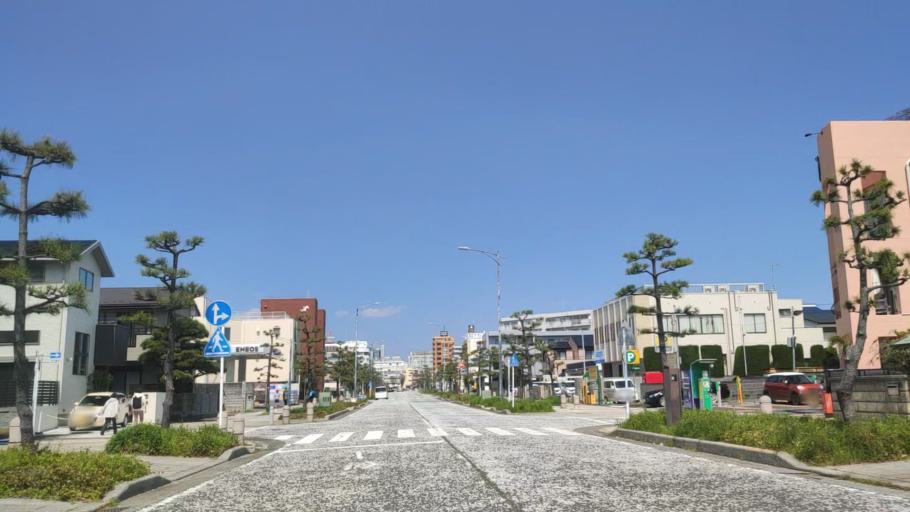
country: JP
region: Kanagawa
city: Hiratsuka
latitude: 35.3222
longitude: 139.3527
